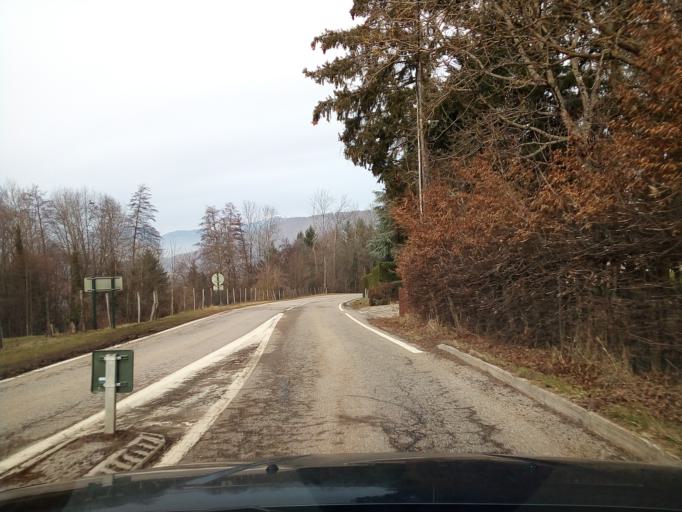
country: FR
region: Rhone-Alpes
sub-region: Departement de l'Isere
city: Revel
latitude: 45.1473
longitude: 5.8556
